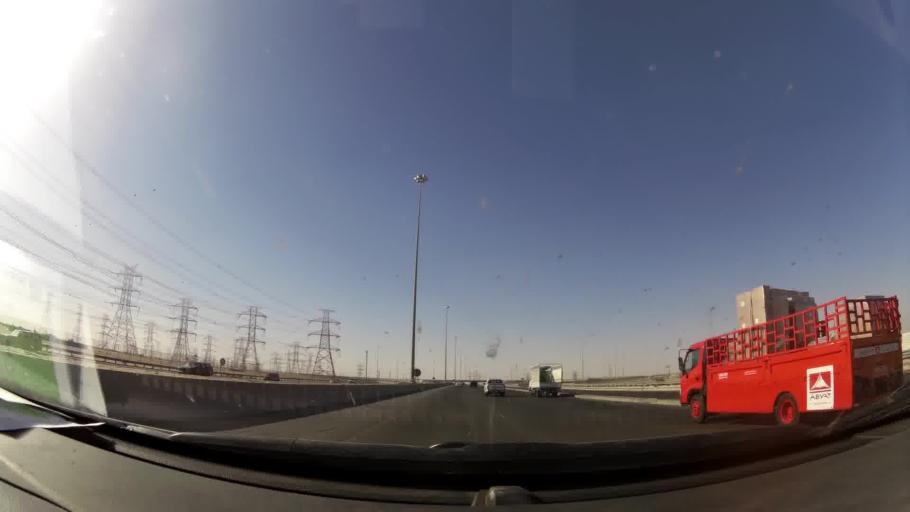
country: KW
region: Muhafazat al Jahra'
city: Al Jahra'
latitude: 29.3022
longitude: 47.6833
